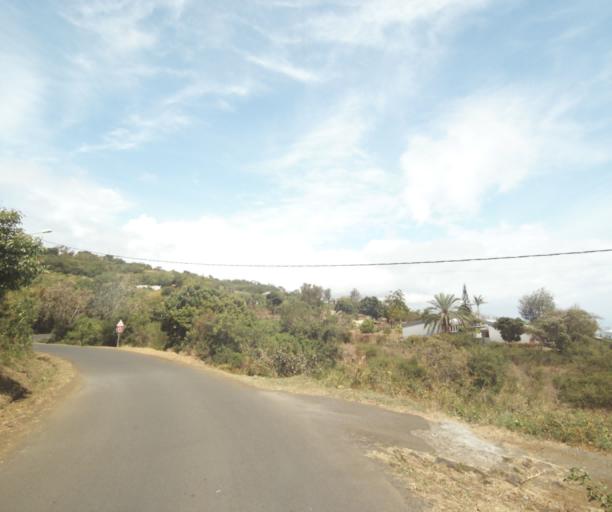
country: RE
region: Reunion
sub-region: Reunion
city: Trois-Bassins
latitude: -21.0967
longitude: 55.2766
